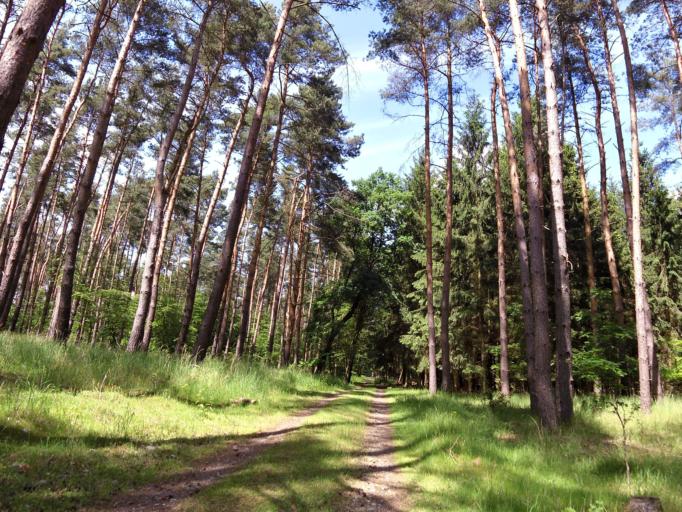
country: DE
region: Hesse
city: Morfelden-Walldorf
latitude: 50.0182
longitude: 8.5460
